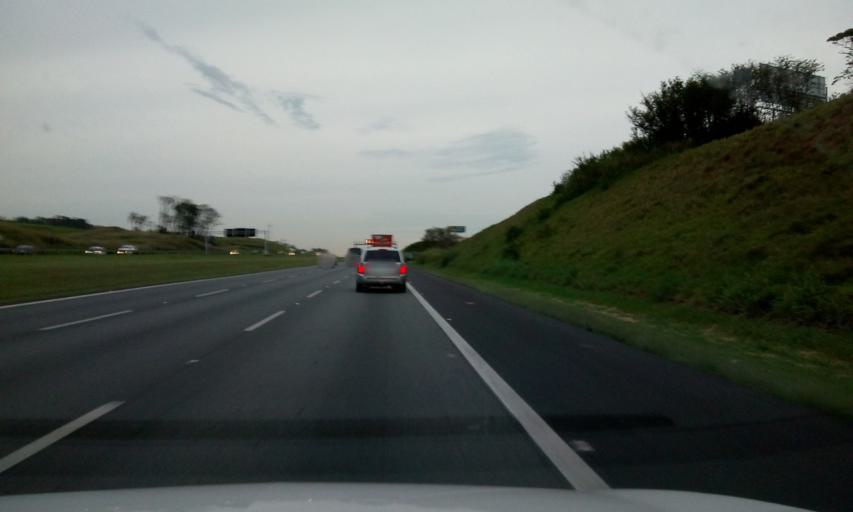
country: BR
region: Sao Paulo
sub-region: Vinhedo
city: Vinhedo
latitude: -23.0488
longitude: -47.0537
